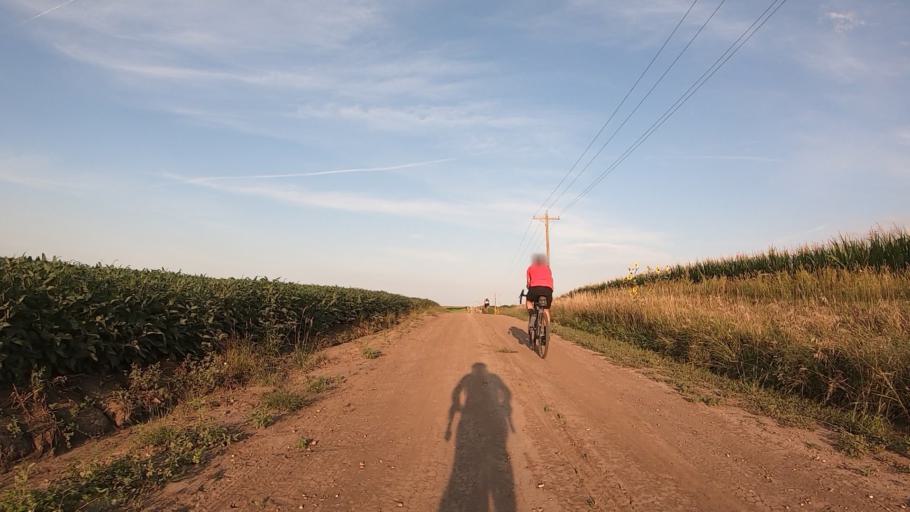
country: US
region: Kansas
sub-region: Marshall County
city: Marysville
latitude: 39.7694
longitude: -96.7260
